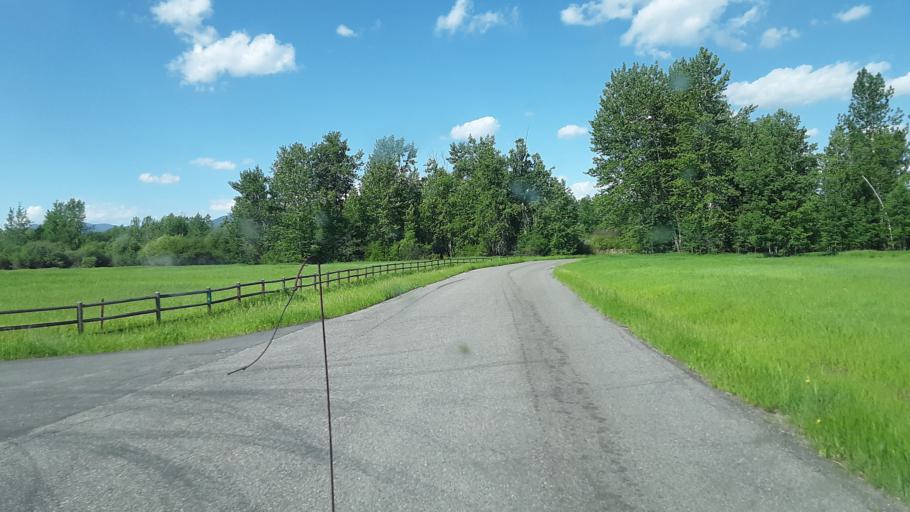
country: US
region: Montana
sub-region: Carbon County
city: Red Lodge
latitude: 45.2767
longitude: -109.2135
